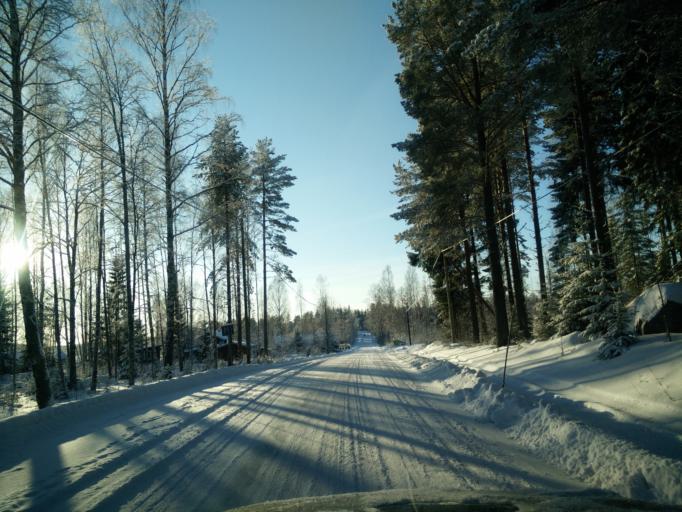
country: SE
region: Vaesternorrland
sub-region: Sundsvalls Kommun
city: Njurundabommen
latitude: 62.2305
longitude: 17.5038
